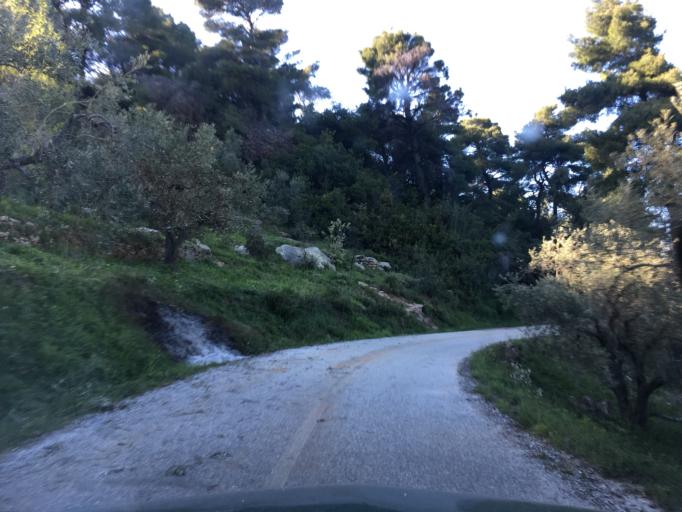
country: GR
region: Thessaly
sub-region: Nomos Magnisias
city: Skopelos
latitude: 39.1843
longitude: 23.6188
